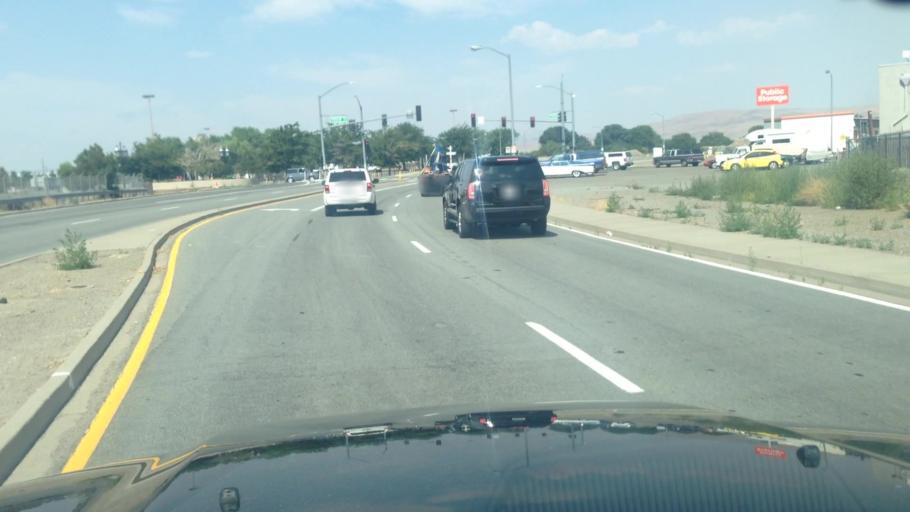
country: US
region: Nevada
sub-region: Washoe County
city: Sparks
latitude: 39.5195
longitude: -119.7750
